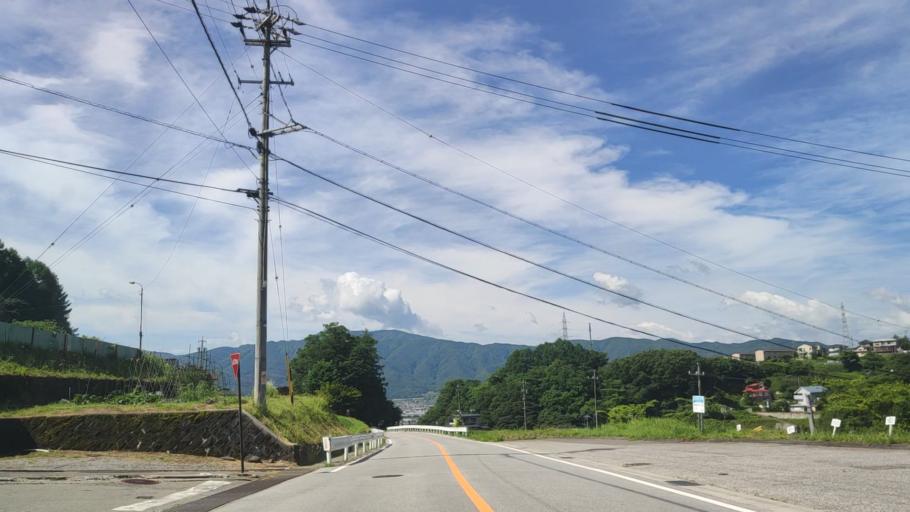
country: JP
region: Nagano
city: Suwa
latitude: 36.0513
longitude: 138.1280
